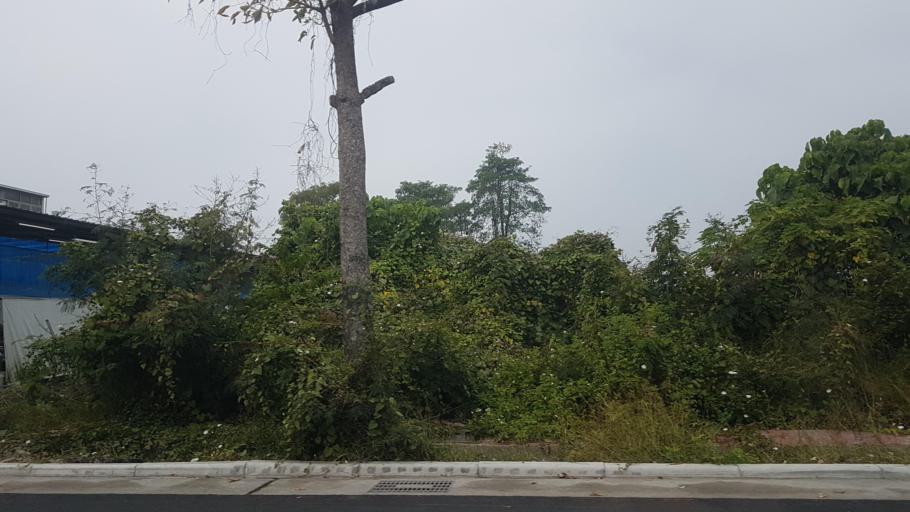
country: TW
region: Taiwan
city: Xinying
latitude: 23.3127
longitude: 120.2990
